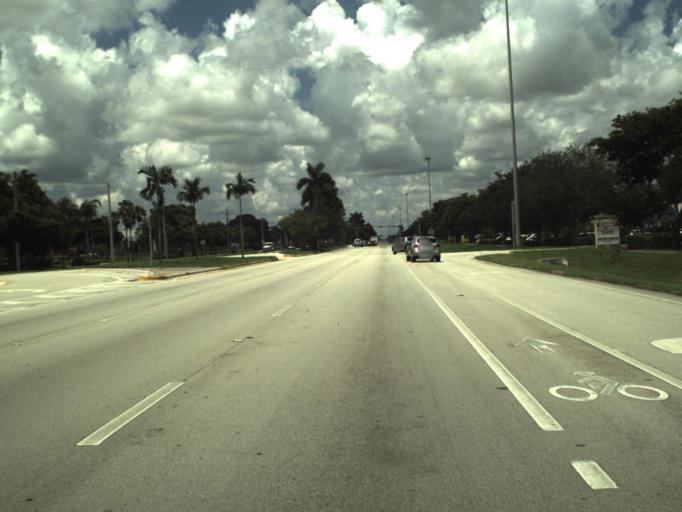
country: US
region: Florida
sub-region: Broward County
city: Pembroke Pines
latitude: 26.0091
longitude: -80.2543
